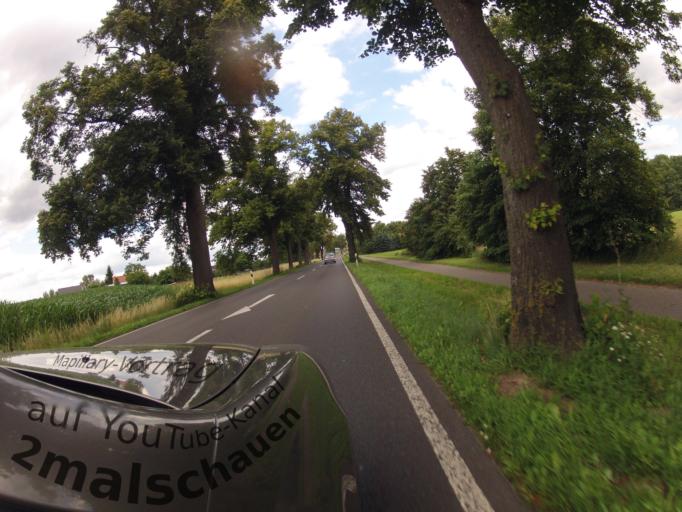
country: DE
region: Mecklenburg-Vorpommern
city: Anklam
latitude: 53.8854
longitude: 13.7024
